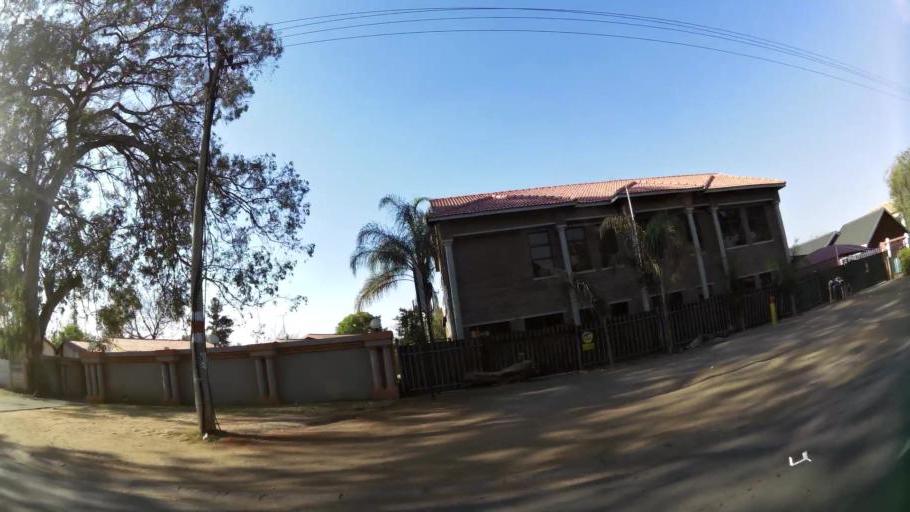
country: ZA
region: North-West
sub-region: Bojanala Platinum District Municipality
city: Rustenburg
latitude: -25.6508
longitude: 27.2285
